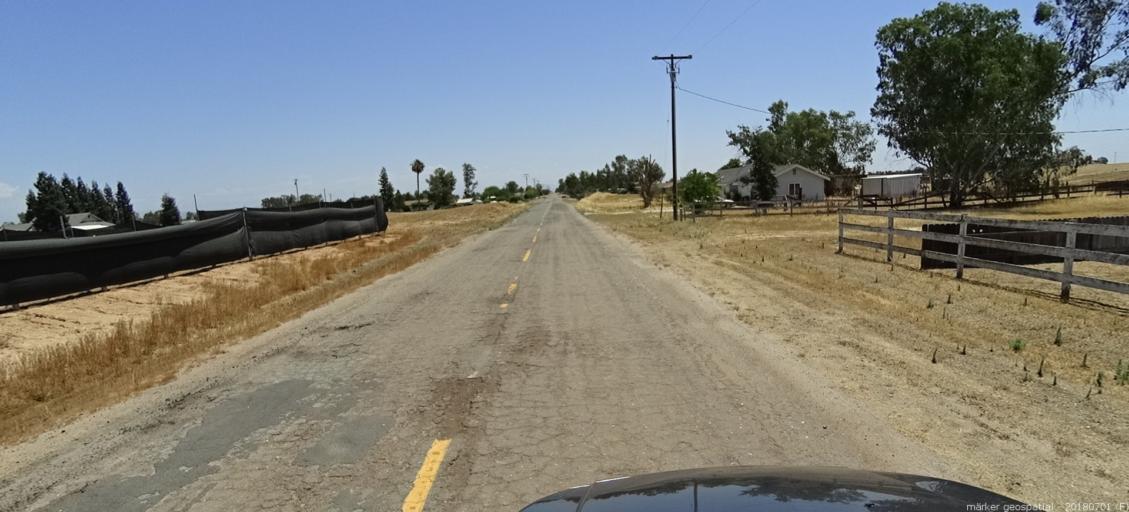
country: US
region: California
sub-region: Madera County
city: Madera Acres
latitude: 37.0336
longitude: -119.9976
